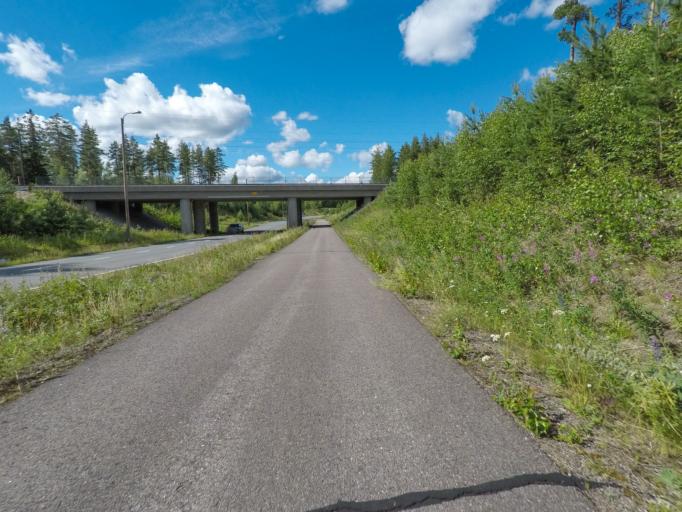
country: FI
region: South Karelia
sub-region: Lappeenranta
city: Joutseno
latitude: 61.0915
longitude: 28.3535
